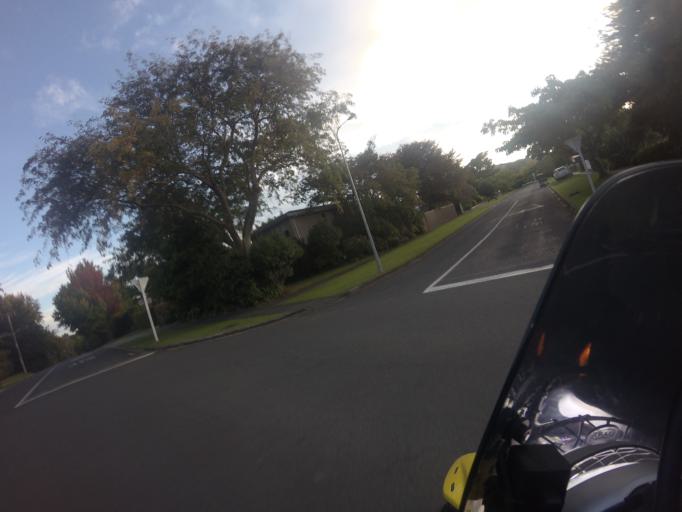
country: NZ
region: Gisborne
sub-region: Gisborne District
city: Gisborne
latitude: -38.6679
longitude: 178.0418
